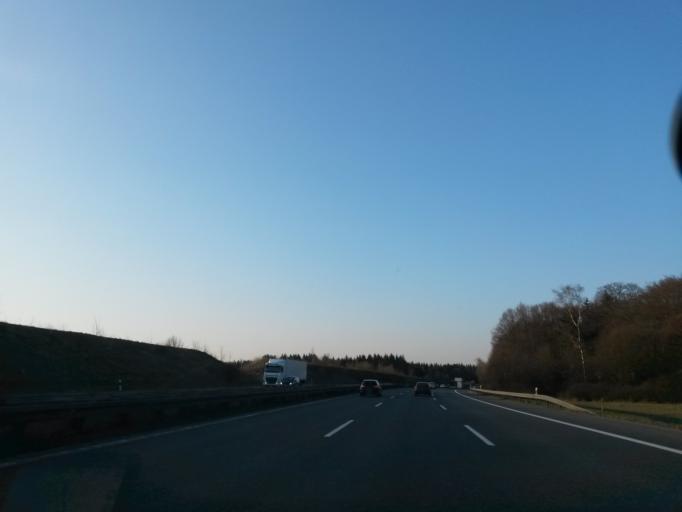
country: DE
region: Bavaria
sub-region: Upper Bavaria
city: Stammham
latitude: 48.8792
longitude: 11.4670
